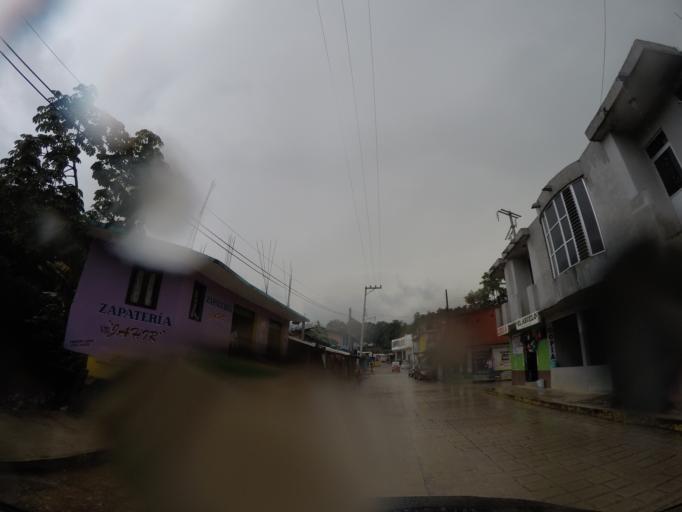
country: MX
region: Oaxaca
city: San Gabriel Mixtepec
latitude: 16.0946
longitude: -97.0816
